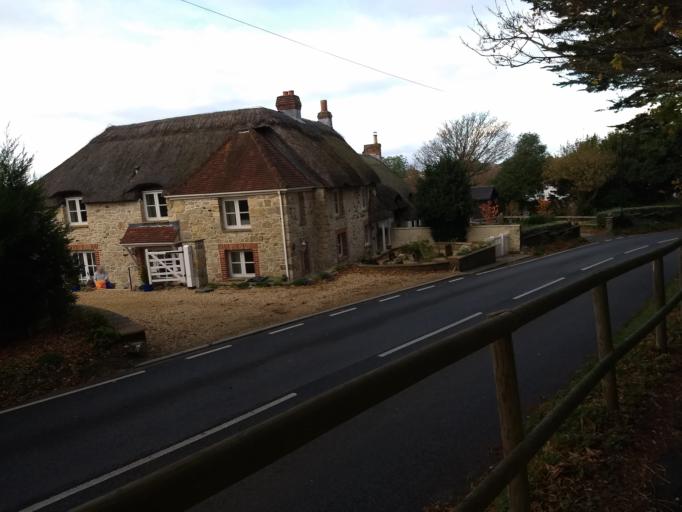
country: GB
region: England
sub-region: Isle of Wight
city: Freshwater
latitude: 50.6994
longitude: -1.5161
